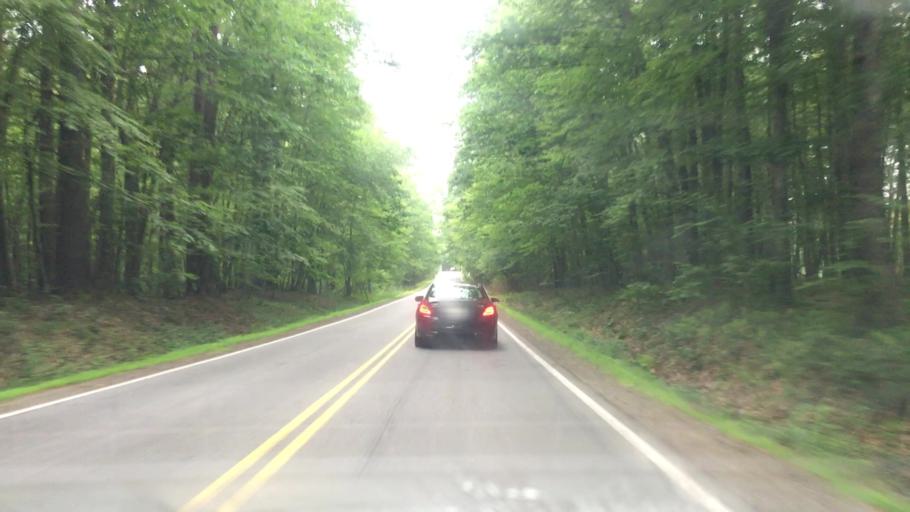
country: US
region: New Hampshire
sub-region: Rockingham County
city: Greenland
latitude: 43.0919
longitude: -70.8393
